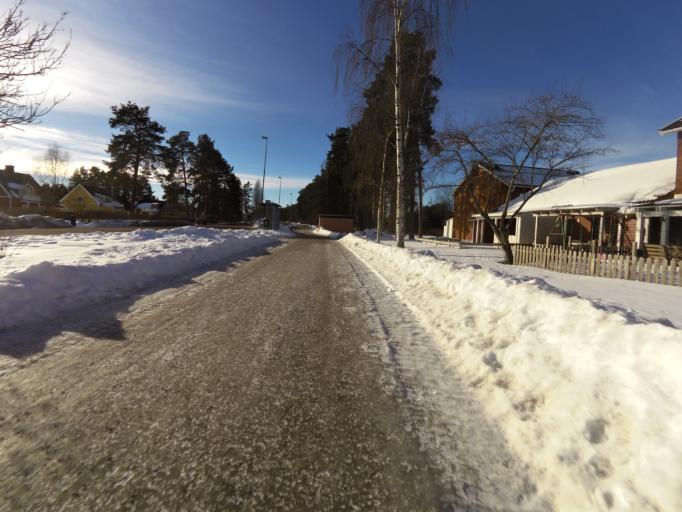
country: SE
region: Gaevleborg
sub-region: Gavle Kommun
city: Valbo
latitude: 60.6399
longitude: 16.9984
